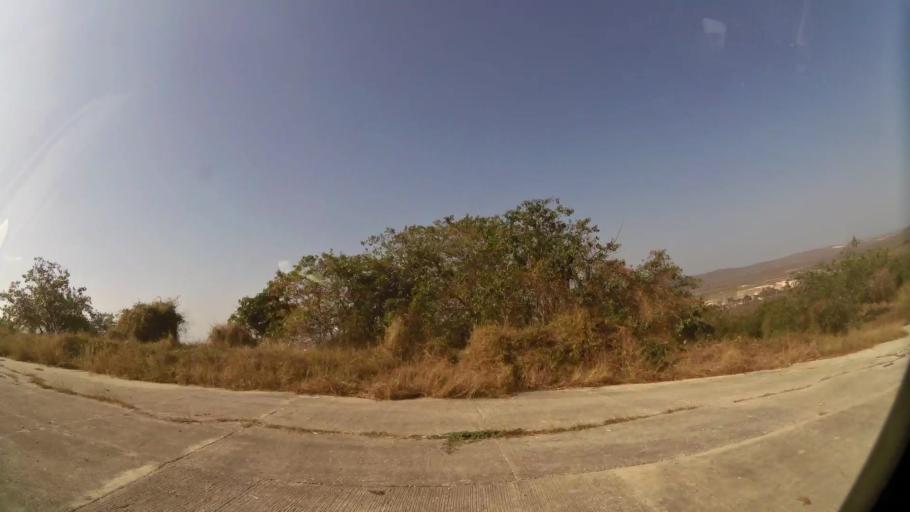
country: CO
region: Atlantico
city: Barranquilla
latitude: 10.9925
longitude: -74.8302
